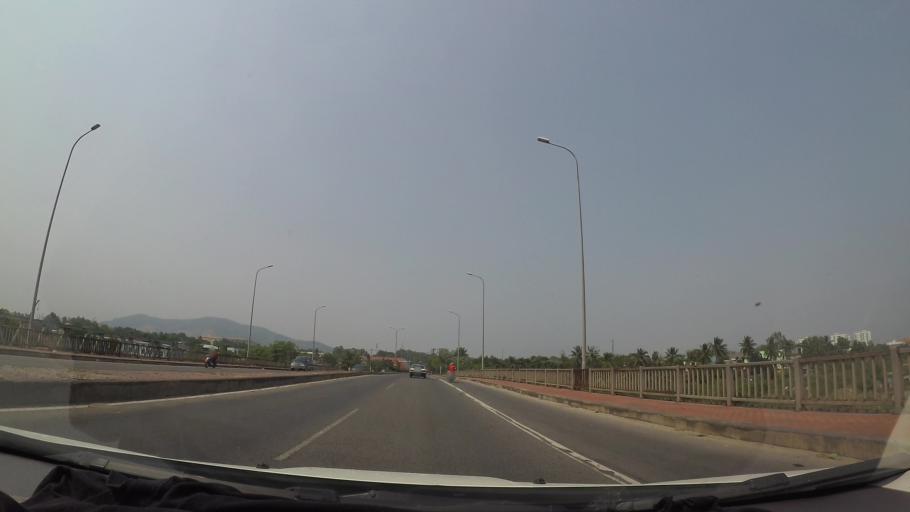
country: VN
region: Da Nang
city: Cam Le
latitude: 15.9999
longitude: 108.1910
